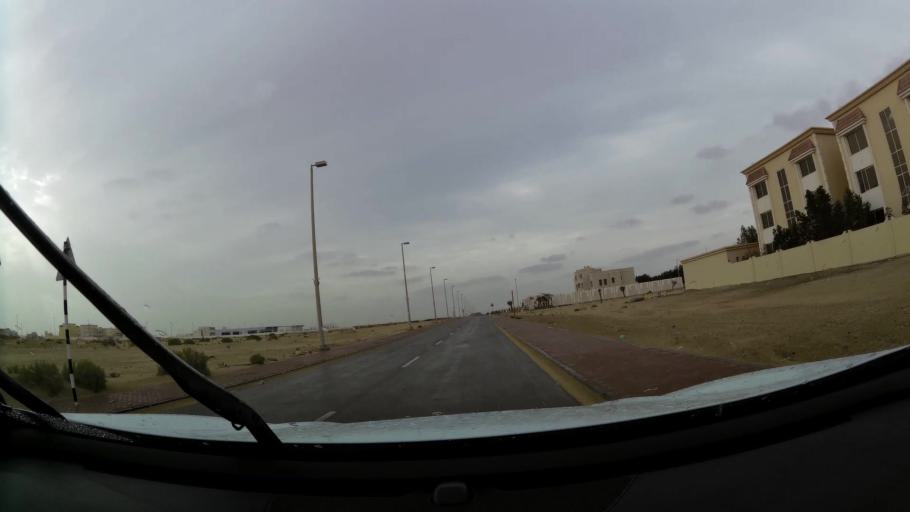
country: AE
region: Abu Dhabi
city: Abu Dhabi
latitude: 24.3679
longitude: 54.6291
